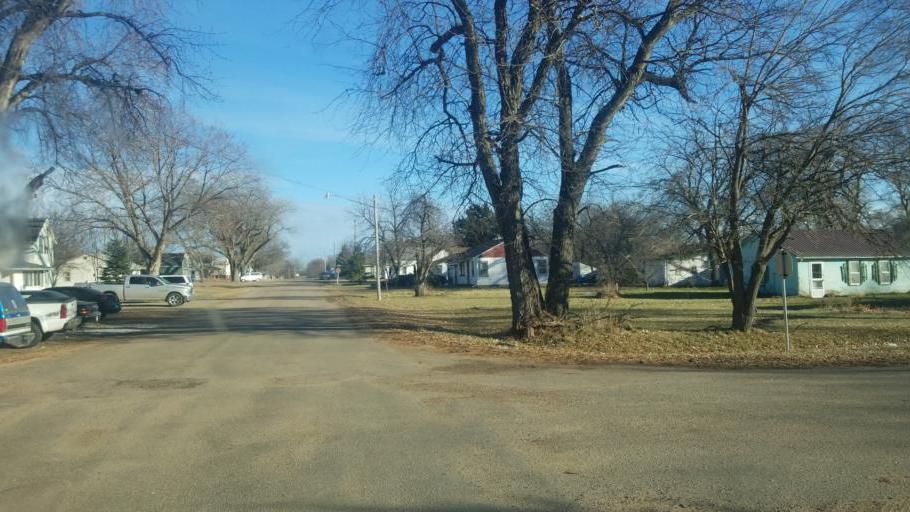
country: US
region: South Dakota
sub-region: Charles Mix County
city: Wagner
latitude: 42.8293
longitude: -98.4698
